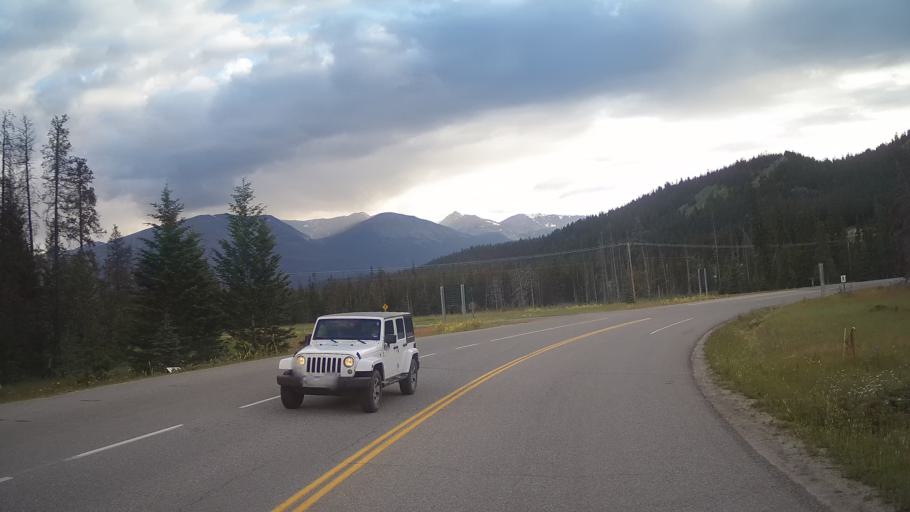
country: CA
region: Alberta
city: Jasper Park Lodge
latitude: 52.9101
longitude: -118.0551
